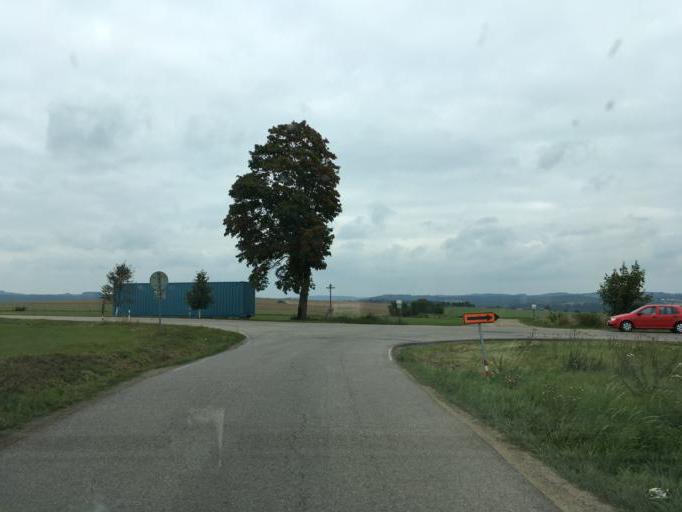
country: CZ
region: Central Bohemia
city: Vlasim
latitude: 49.7249
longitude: 14.8874
